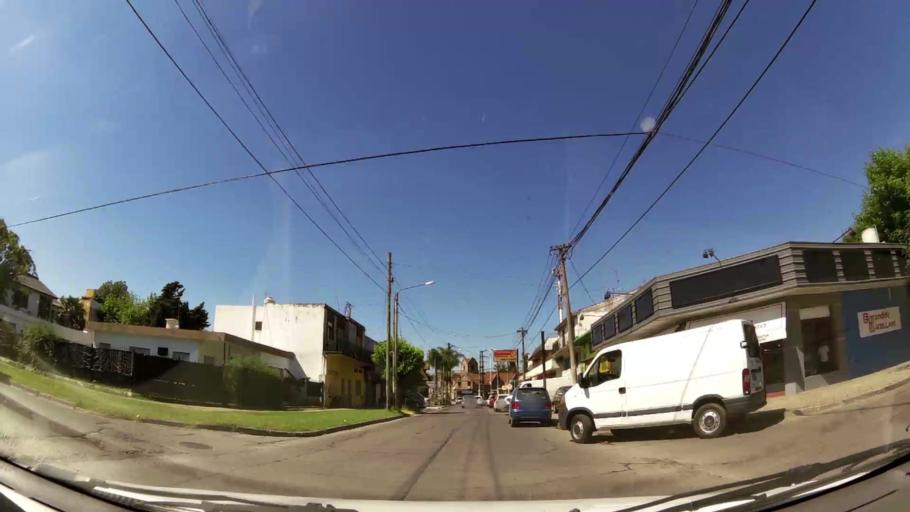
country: AR
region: Buenos Aires
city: Ituzaingo
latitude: -34.6473
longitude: -58.6643
